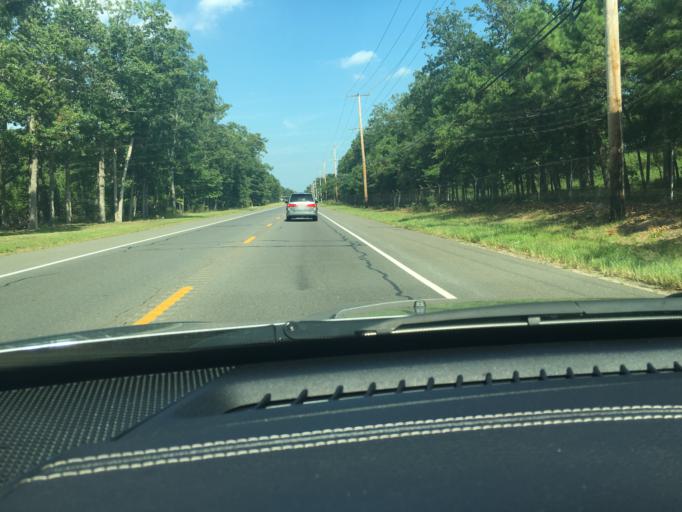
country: US
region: New Jersey
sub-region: Ocean County
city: Leisure Village West-Pine Lake Park
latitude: 40.0281
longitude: -74.2603
